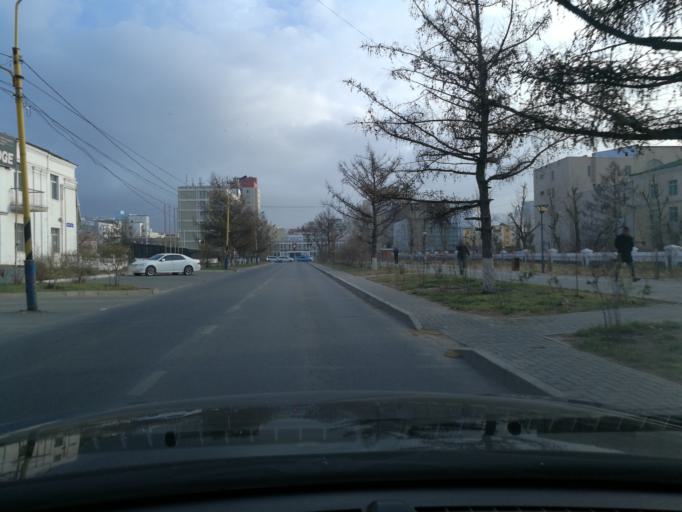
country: MN
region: Ulaanbaatar
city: Ulaanbaatar
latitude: 47.9244
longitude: 106.9275
